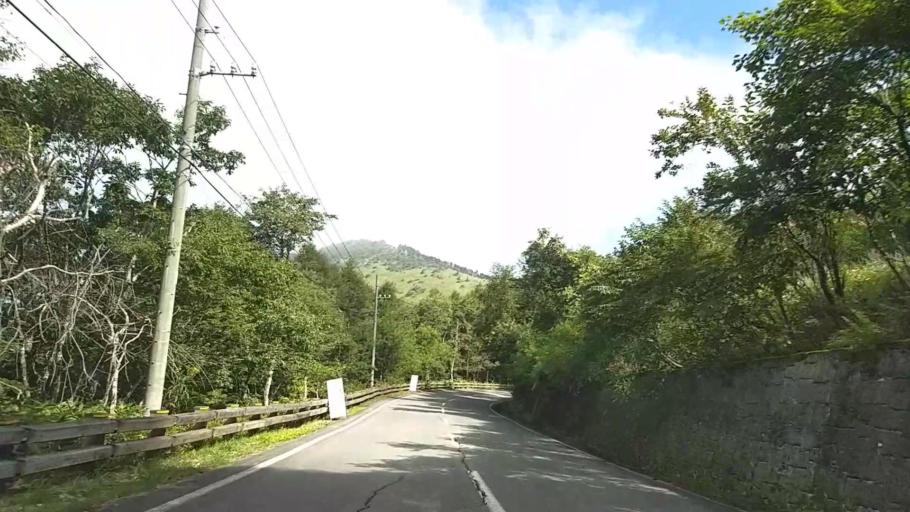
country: JP
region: Nagano
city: Suwa
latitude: 36.1183
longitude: 138.1586
